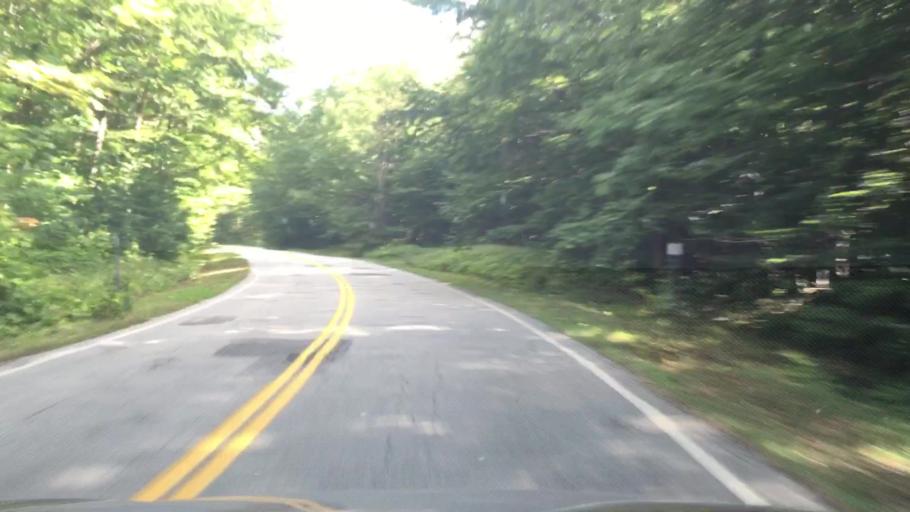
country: US
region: New Hampshire
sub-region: Carroll County
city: Tamworth
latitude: 44.0280
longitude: -71.3227
